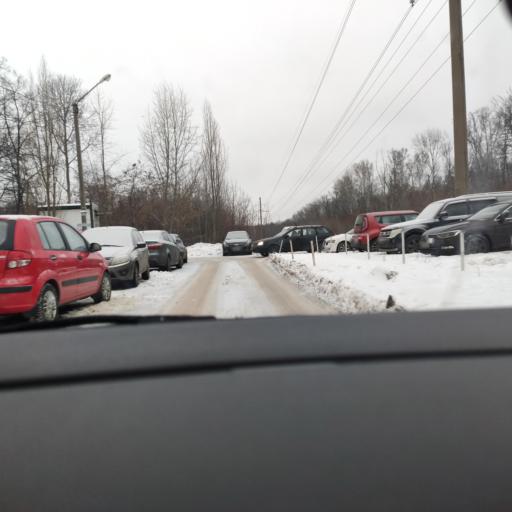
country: RU
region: Voronezj
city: Podgornoye
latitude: 51.7321
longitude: 39.2030
